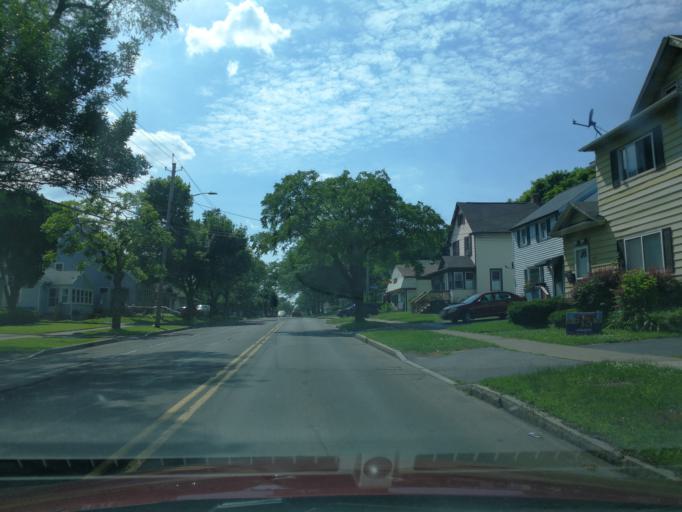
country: US
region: New York
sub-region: Monroe County
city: Irondequoit
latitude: 43.1873
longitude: -77.5887
